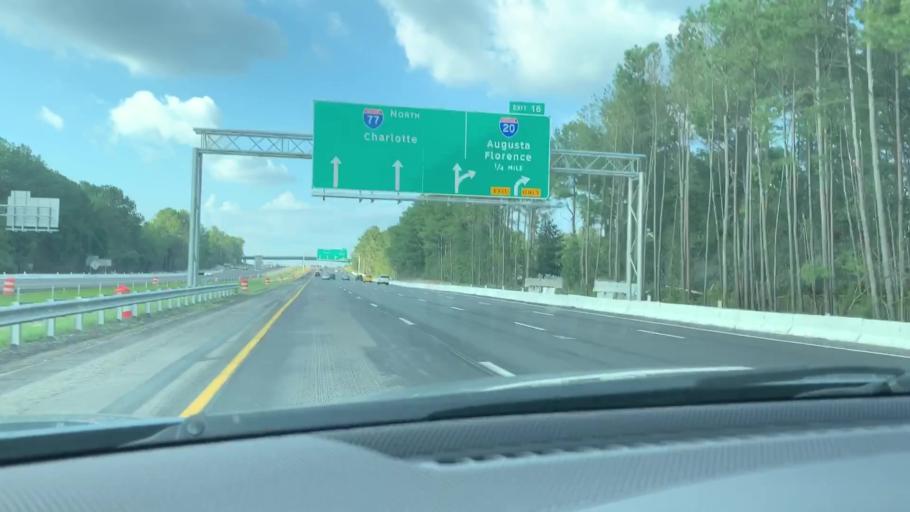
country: US
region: South Carolina
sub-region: Richland County
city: Woodfield
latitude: 34.0578
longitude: -80.9221
